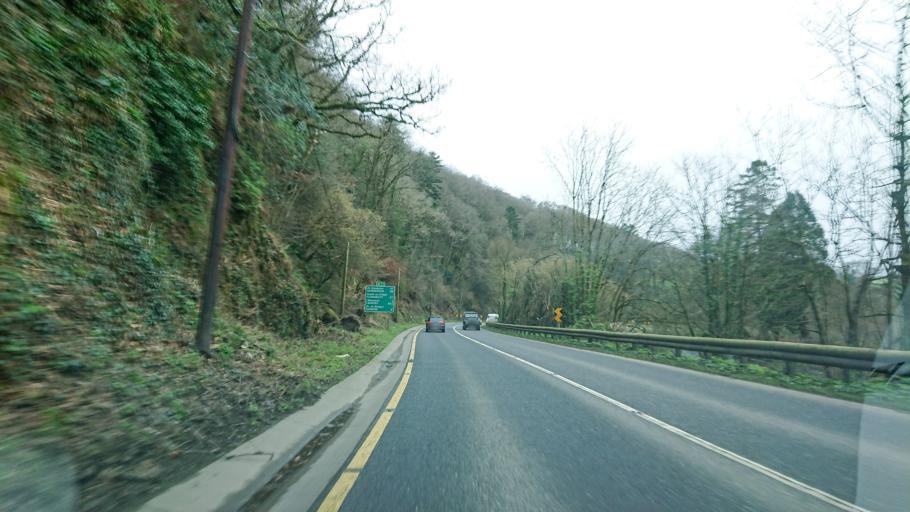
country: IE
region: Munster
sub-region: County Cork
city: Bandon
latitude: 51.7662
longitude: -8.6791
